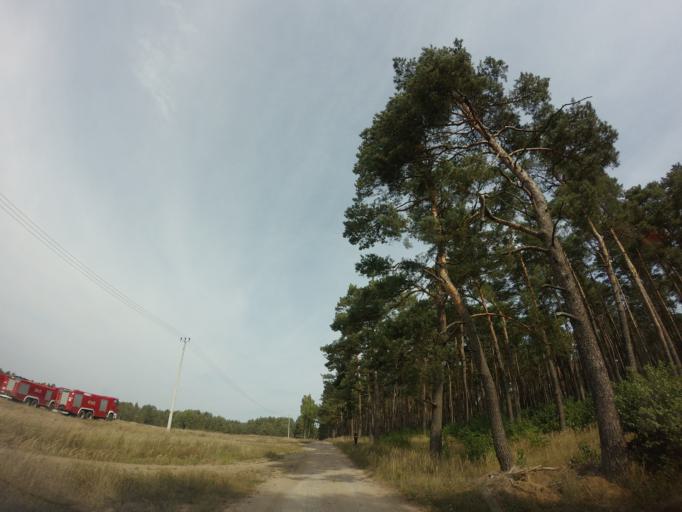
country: PL
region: West Pomeranian Voivodeship
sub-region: Powiat drawski
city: Drawsko Pomorskie
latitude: 53.4675
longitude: 15.7138
